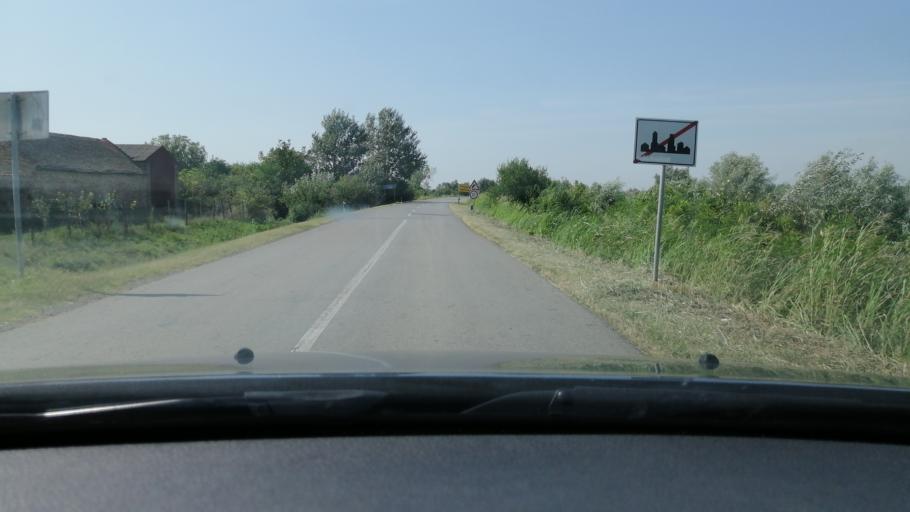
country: RS
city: Tomasevac
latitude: 45.2599
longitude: 20.6170
